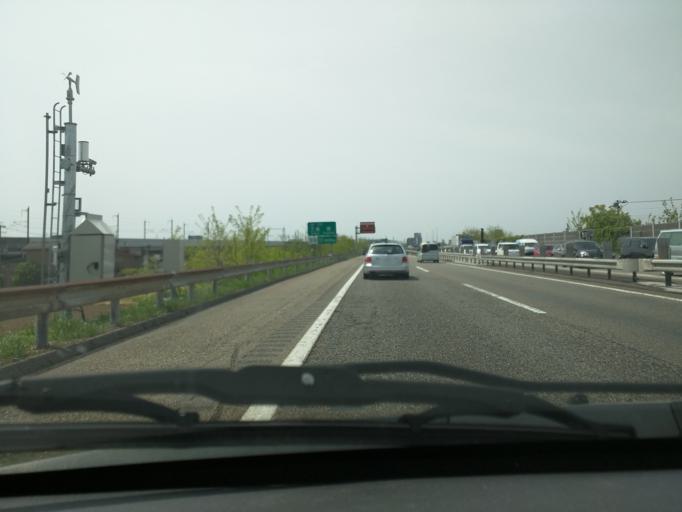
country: JP
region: Niigata
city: Tsubame
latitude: 37.6583
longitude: 138.9426
